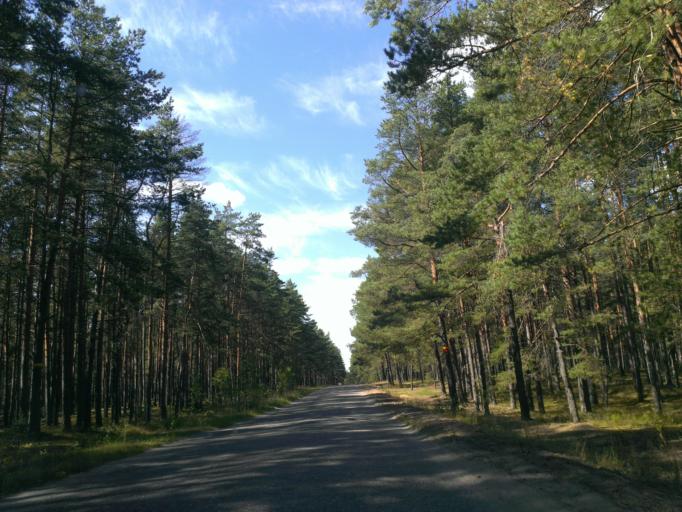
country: LV
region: Garkalne
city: Garkalne
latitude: 57.1031
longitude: 24.3873
